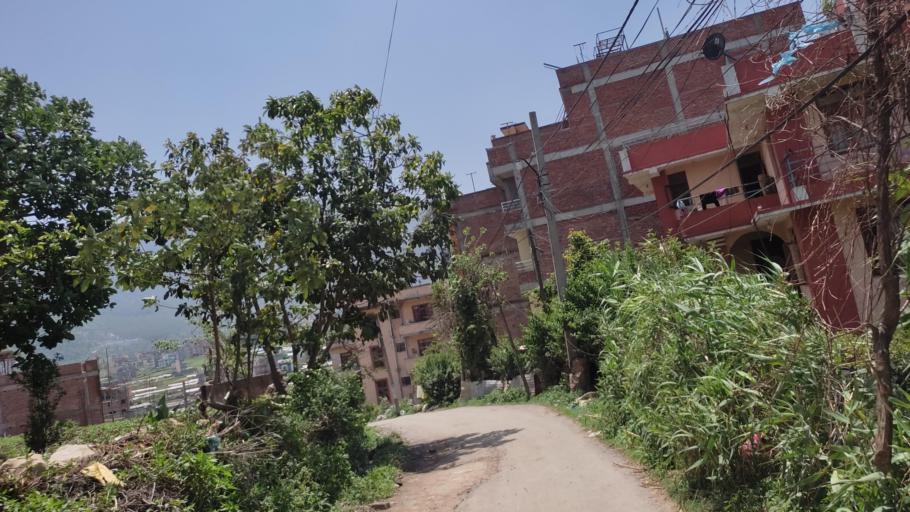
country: NP
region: Central Region
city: Kirtipur
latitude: 27.6761
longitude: 85.2713
